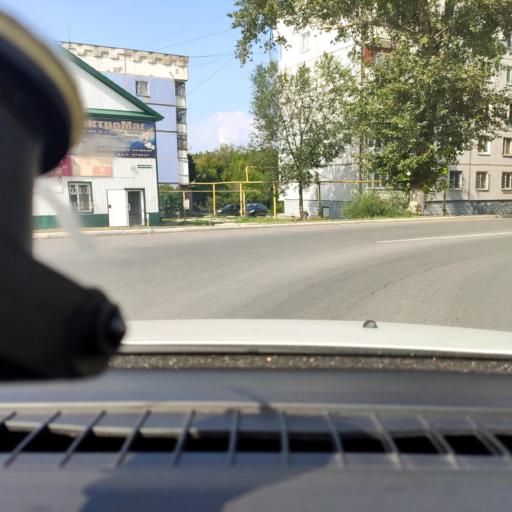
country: RU
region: Samara
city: Chapayevsk
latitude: 52.9576
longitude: 49.6804
